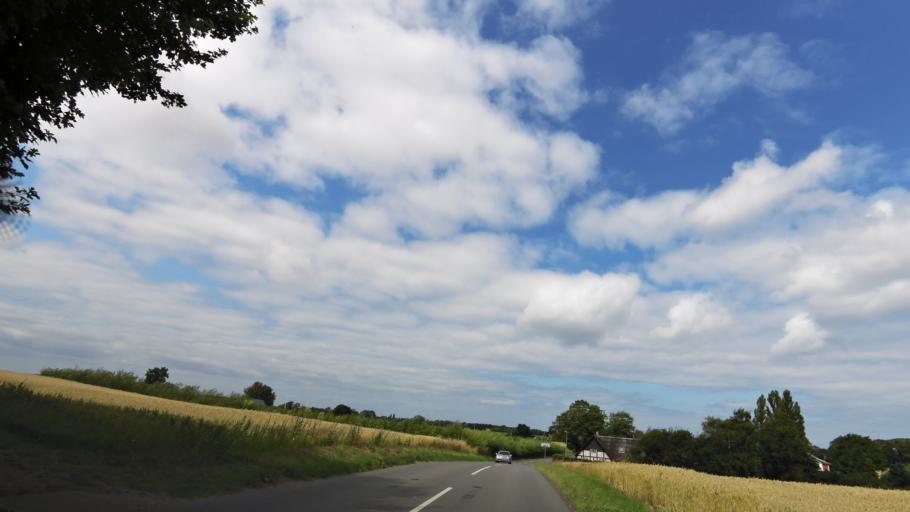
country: DK
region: South Denmark
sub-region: Nordfyns Kommune
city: Otterup
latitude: 55.5705
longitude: 10.3911
